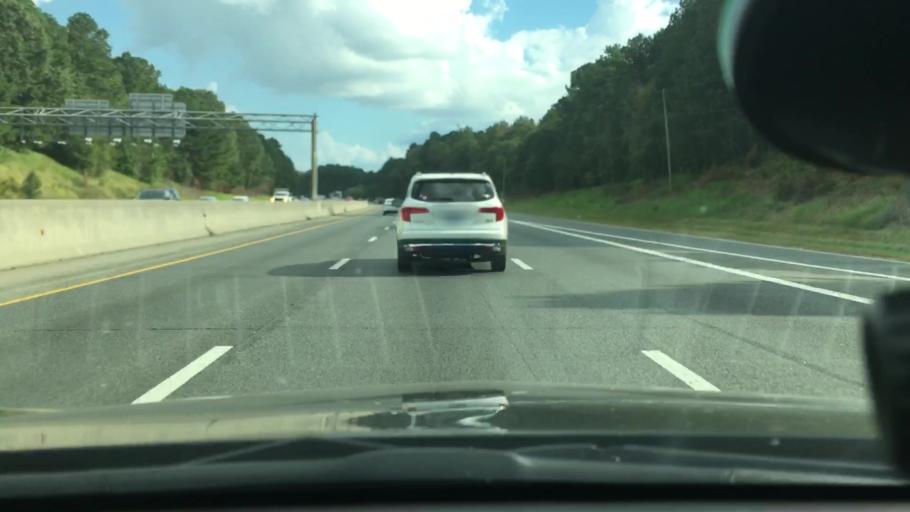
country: US
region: North Carolina
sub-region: Orange County
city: Chapel Hill
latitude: 35.9109
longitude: -78.9802
